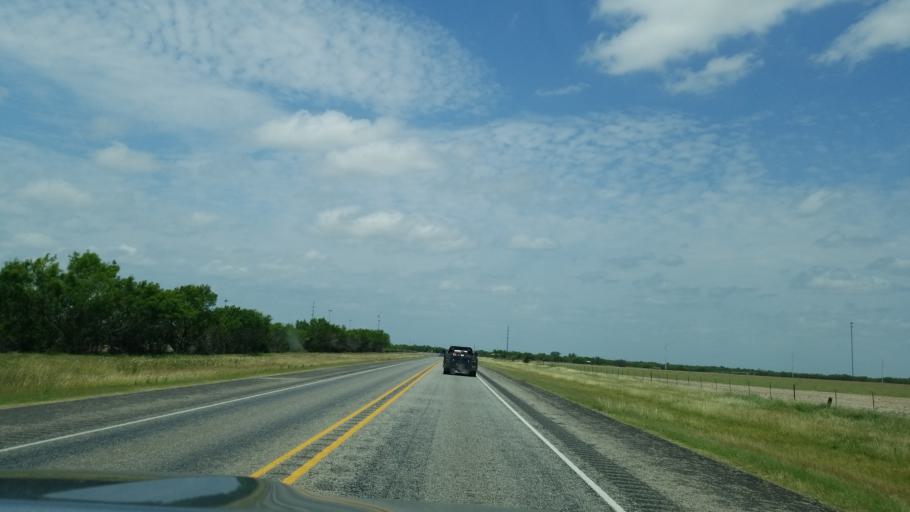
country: US
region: Texas
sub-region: Zavala County
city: La Pryor
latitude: 28.9428
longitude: -99.8280
